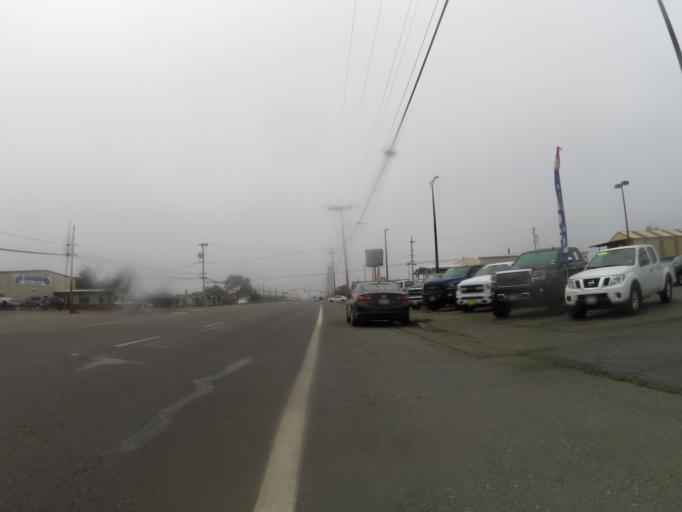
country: US
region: California
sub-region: Del Norte County
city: Crescent City
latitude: 41.7701
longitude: -124.1997
